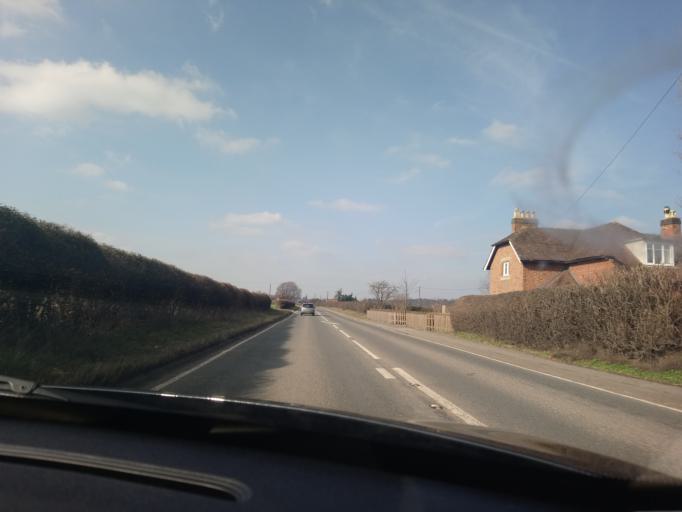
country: GB
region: England
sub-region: Shropshire
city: Berrington
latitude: 52.6851
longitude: -2.6938
